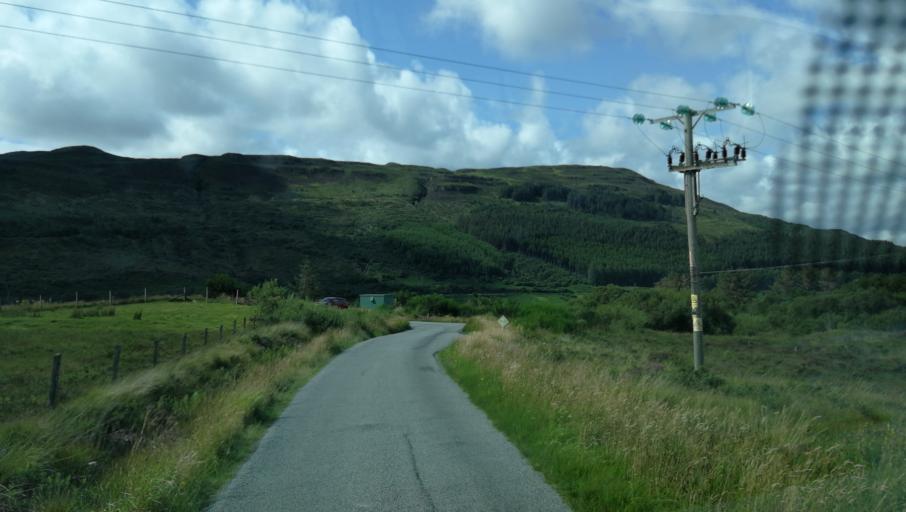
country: GB
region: Scotland
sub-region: Highland
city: Portree
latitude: 57.3855
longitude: -6.1939
